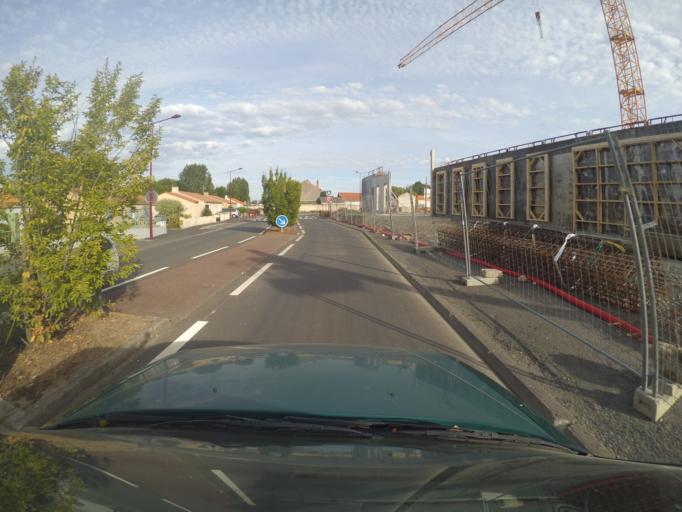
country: FR
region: Pays de la Loire
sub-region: Departement de la Loire-Atlantique
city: Saint-Hilaire-de-Clisson
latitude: 47.0616
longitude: -1.3127
